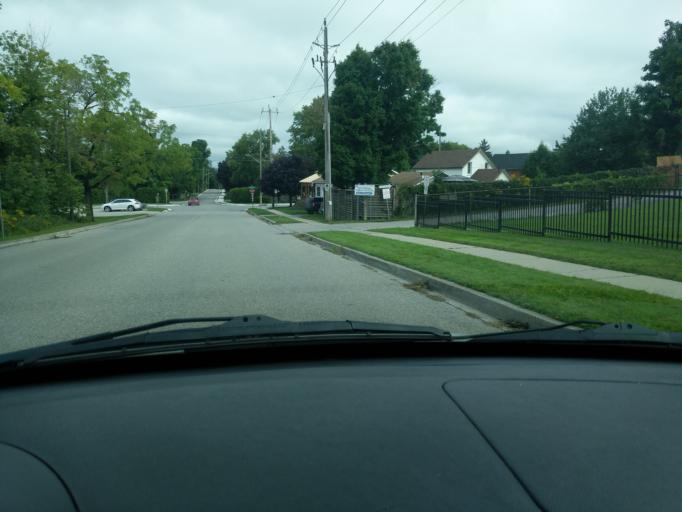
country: CA
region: Ontario
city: Cambridge
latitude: 43.4227
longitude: -80.3201
